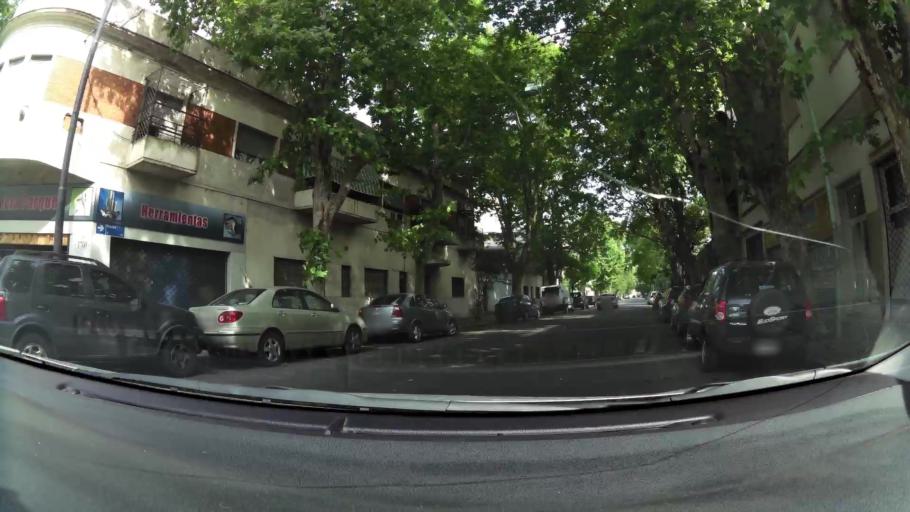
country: AR
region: Buenos Aires F.D.
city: Buenos Aires
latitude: -34.6392
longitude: -58.4171
